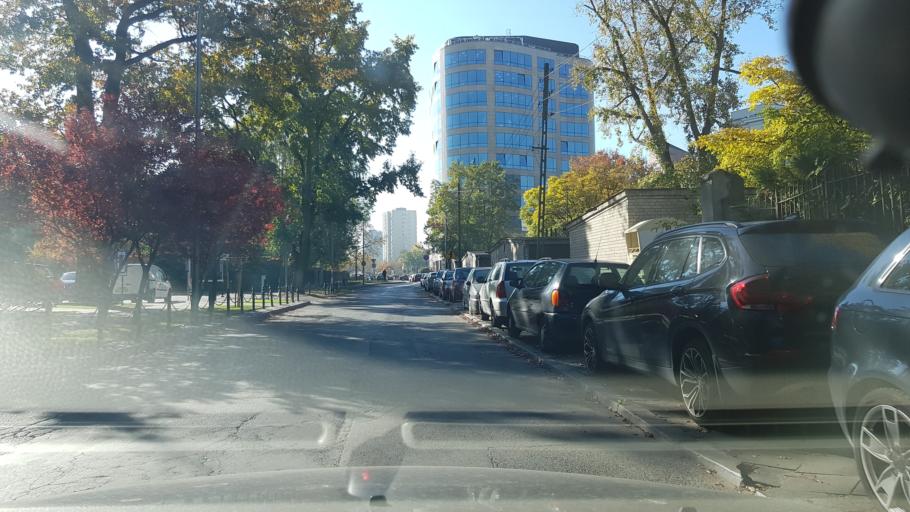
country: PL
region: Masovian Voivodeship
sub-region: Warszawa
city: Mokotow
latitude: 52.1854
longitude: 21.0214
